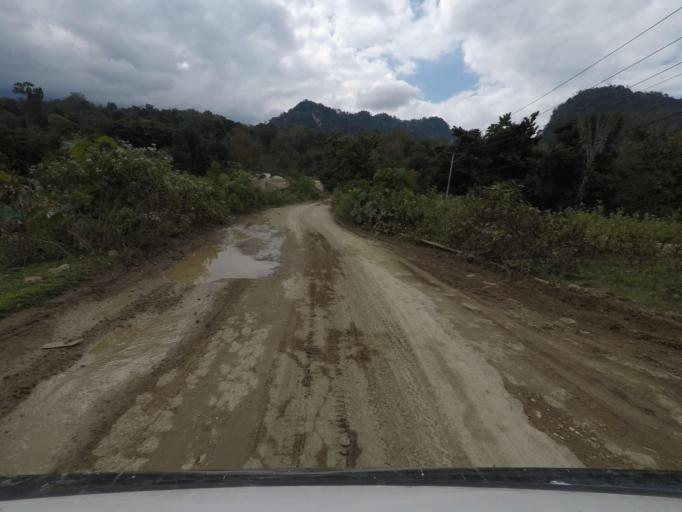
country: TL
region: Viqueque
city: Viqueque
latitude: -8.7806
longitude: 126.3759
